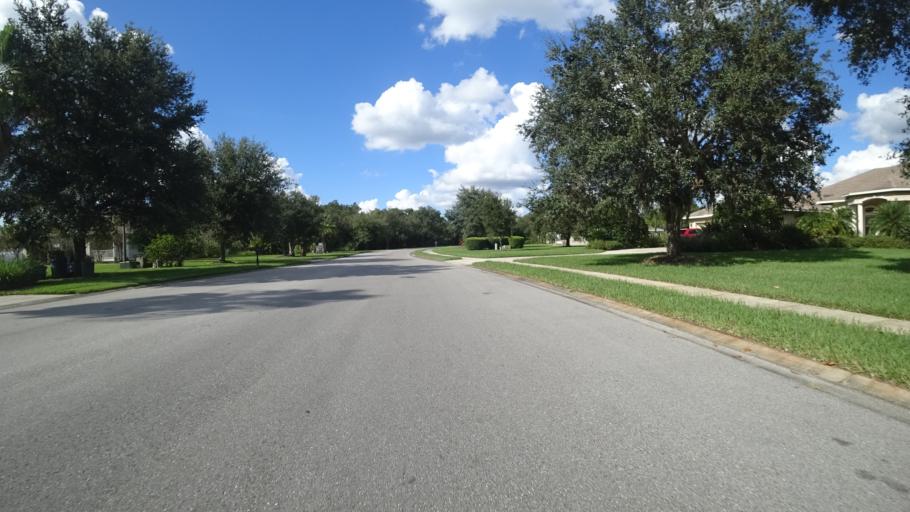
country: US
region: Florida
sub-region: Manatee County
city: Ellenton
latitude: 27.5501
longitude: -82.3862
